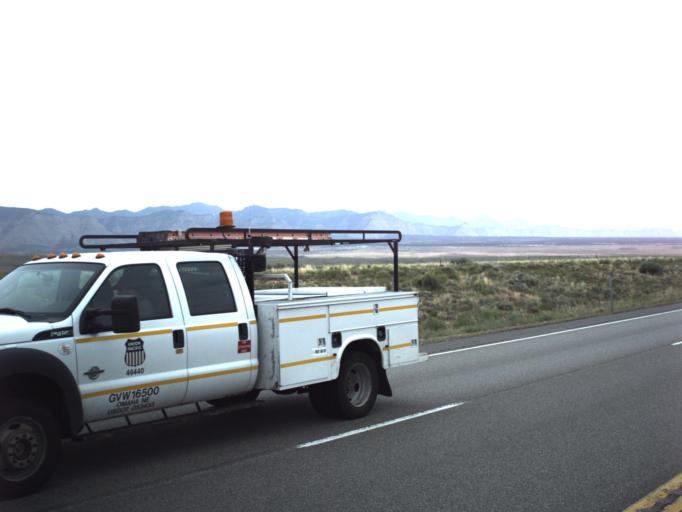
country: US
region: Utah
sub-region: Carbon County
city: East Carbon City
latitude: 39.4876
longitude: -110.5161
